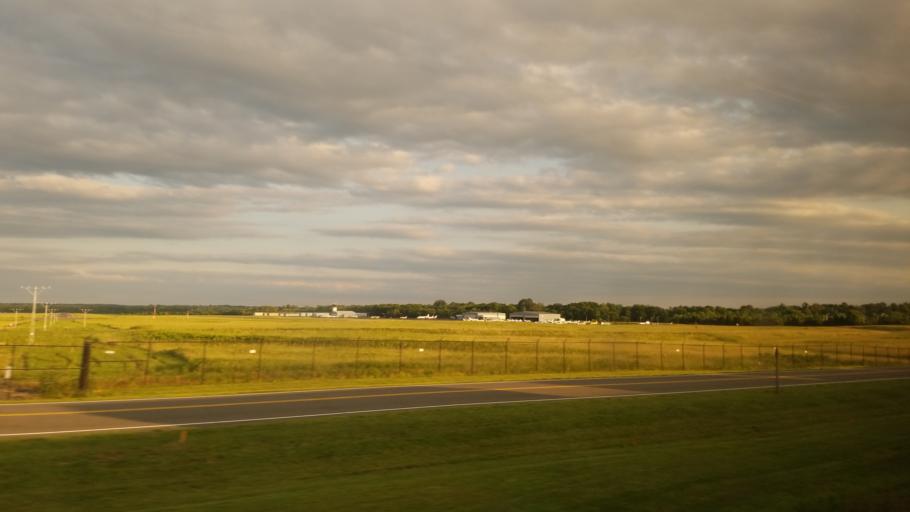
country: US
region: Virginia
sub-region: City of Manassas
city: Manassas
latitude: 38.7320
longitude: -77.5219
